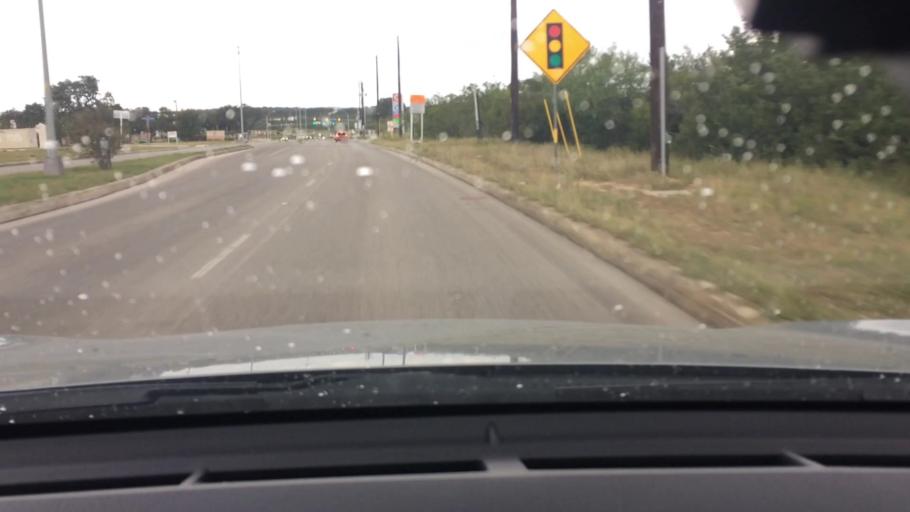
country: US
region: Texas
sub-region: Bexar County
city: Shavano Park
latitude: 29.5893
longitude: -98.5890
